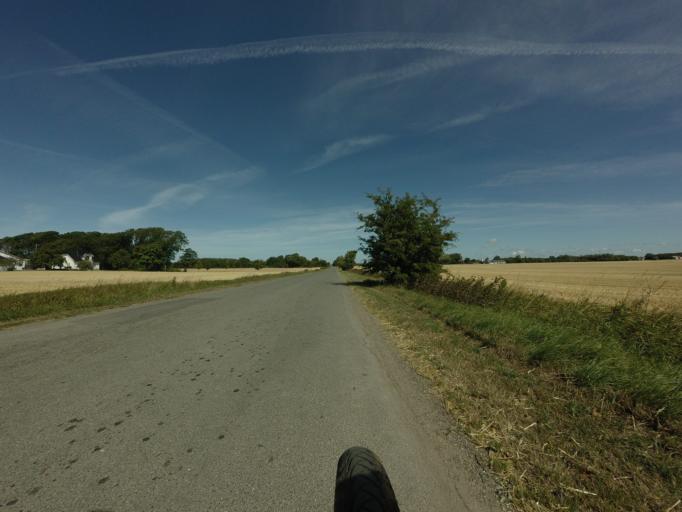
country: DK
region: North Denmark
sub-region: Bronderslev Kommune
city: Bronderslev
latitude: 57.3245
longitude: 9.8203
